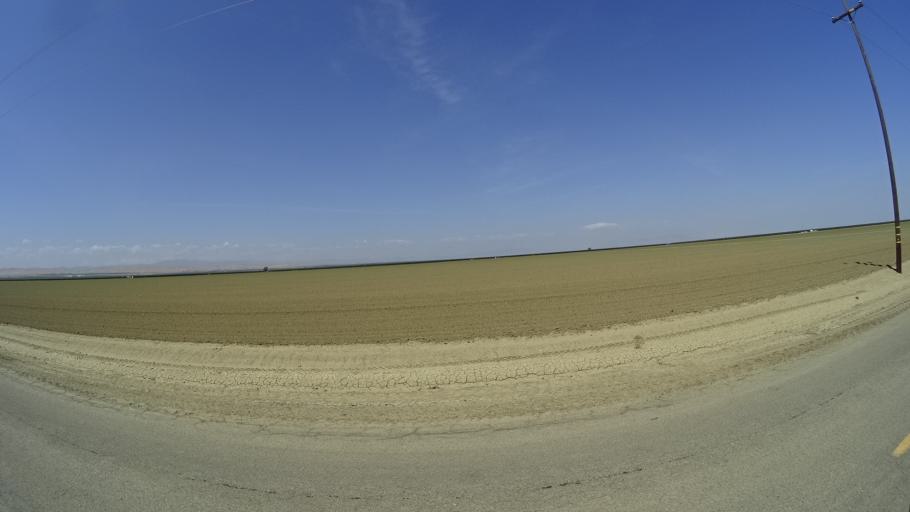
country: US
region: California
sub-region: Kings County
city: Kettleman City
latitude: 36.1149
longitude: -120.0037
